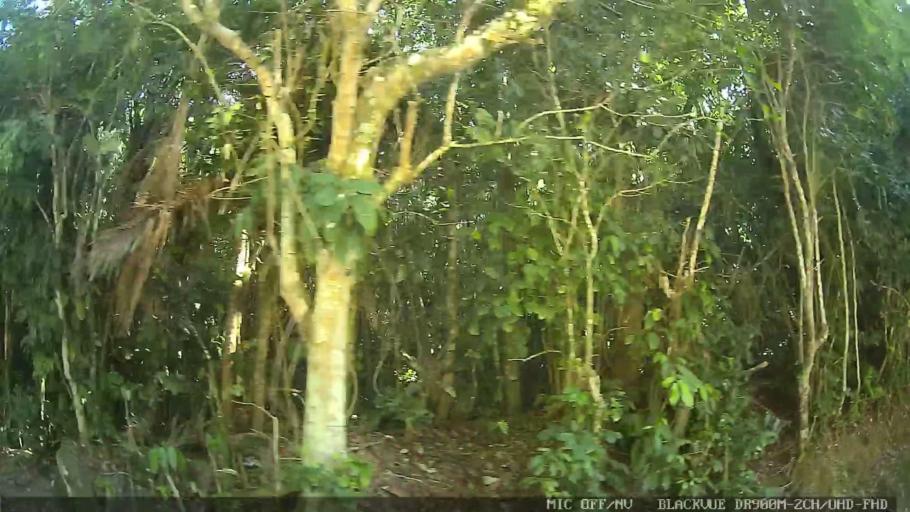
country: BR
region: Sao Paulo
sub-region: Guaruja
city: Guaruja
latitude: -23.9879
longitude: -46.1876
